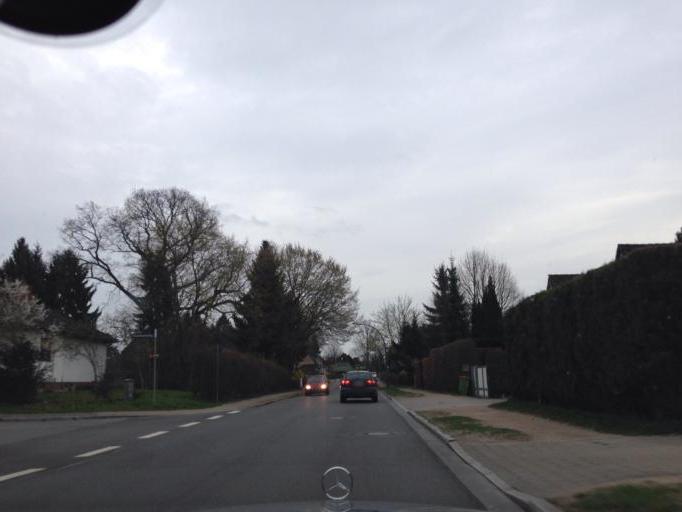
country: DE
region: Hamburg
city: Sasel
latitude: 53.6343
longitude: 10.1365
